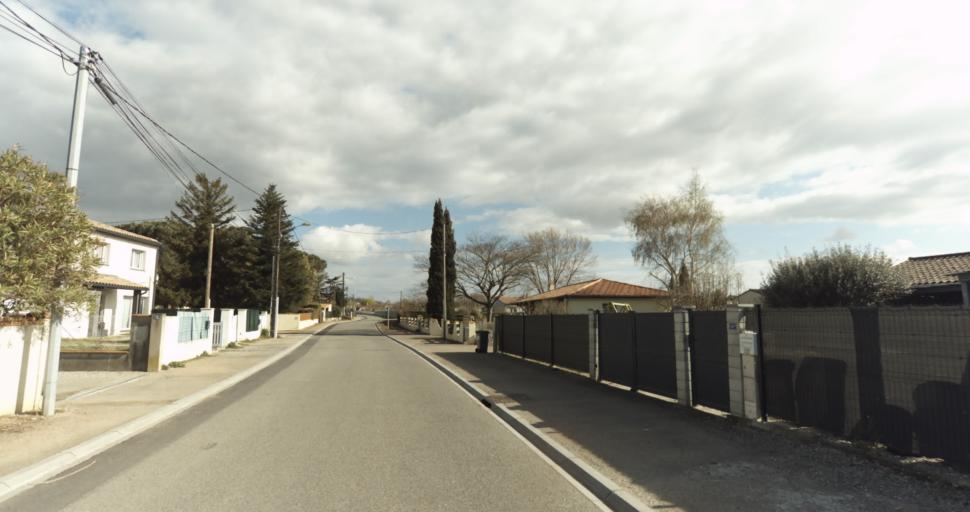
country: FR
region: Midi-Pyrenees
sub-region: Departement de la Haute-Garonne
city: Auterive
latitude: 43.3431
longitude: 1.4877
